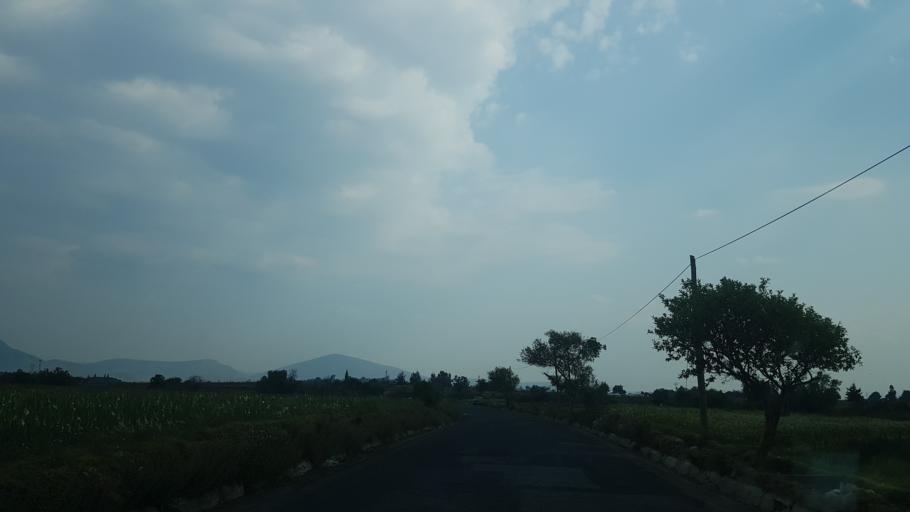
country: MX
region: Puebla
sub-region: Santa Isabel Cholula
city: Santa Ana Acozautla
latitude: 18.9622
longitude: -98.3955
